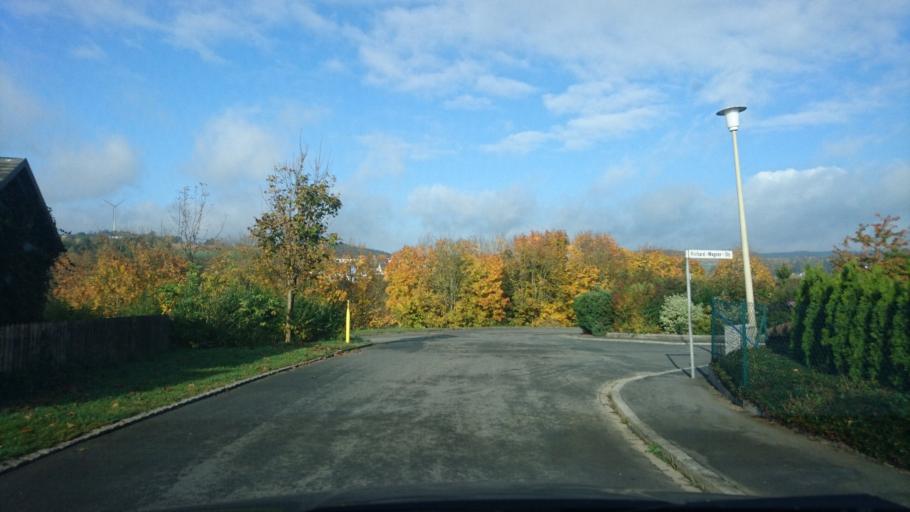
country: DE
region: Bavaria
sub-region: Upper Franconia
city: Selbitz
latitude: 50.3082
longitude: 11.7476
